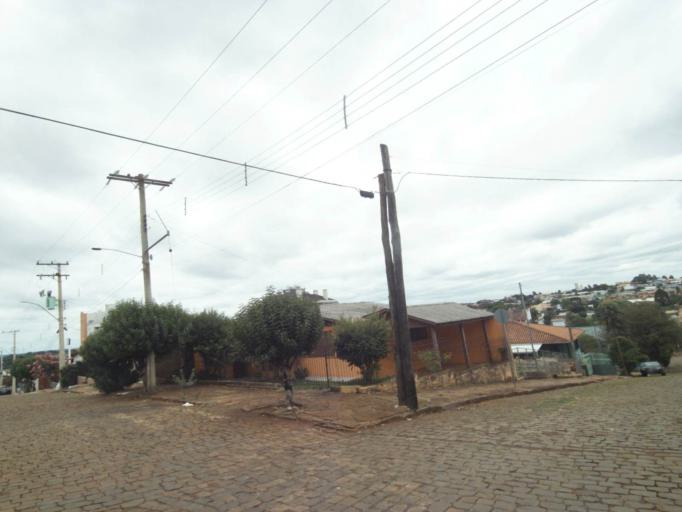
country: BR
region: Rio Grande do Sul
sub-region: Lagoa Vermelha
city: Lagoa Vermelha
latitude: -28.2102
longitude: -51.5191
